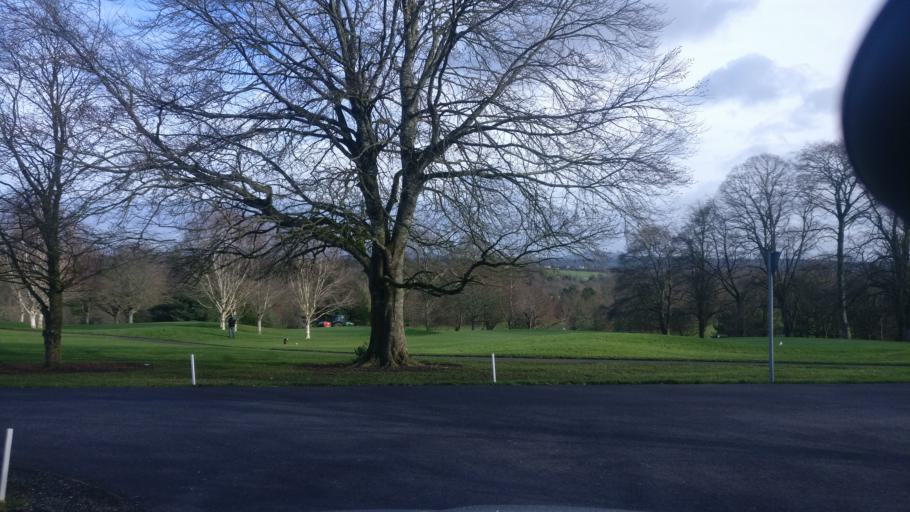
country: IE
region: Leinster
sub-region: Kilkenny
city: Thomastown
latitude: 52.5270
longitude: -7.1878
